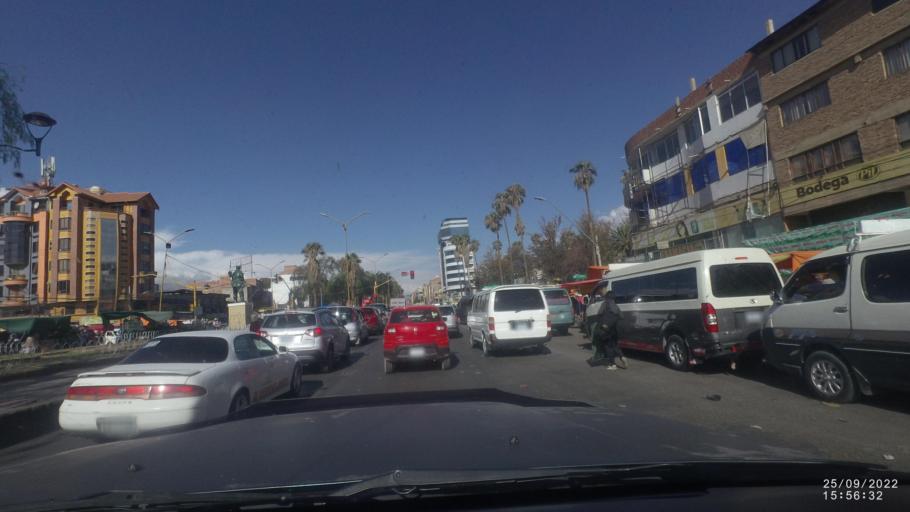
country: BO
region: Cochabamba
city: Sipe Sipe
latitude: -17.3943
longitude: -66.2821
